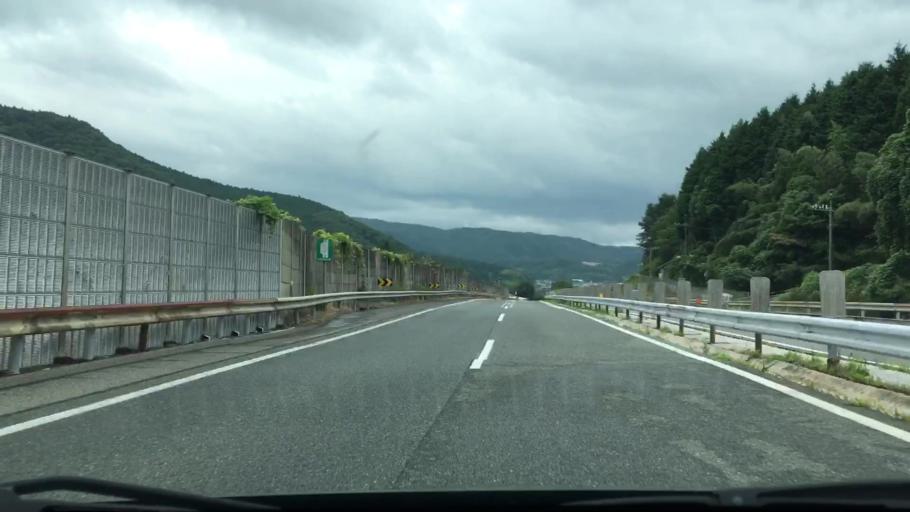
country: JP
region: Okayama
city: Niimi
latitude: 34.9512
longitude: 133.3292
